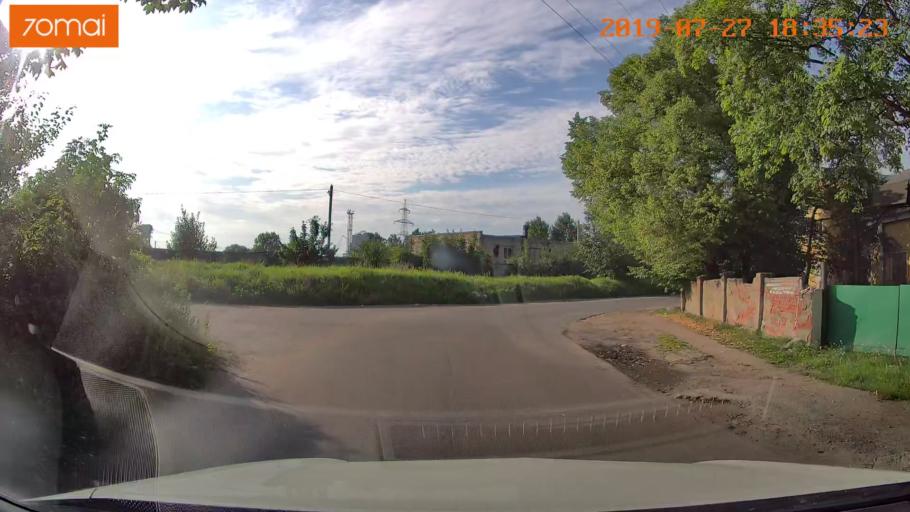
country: RU
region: Kaliningrad
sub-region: Gorod Kaliningrad
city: Kaliningrad
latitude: 54.7039
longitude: 20.4986
